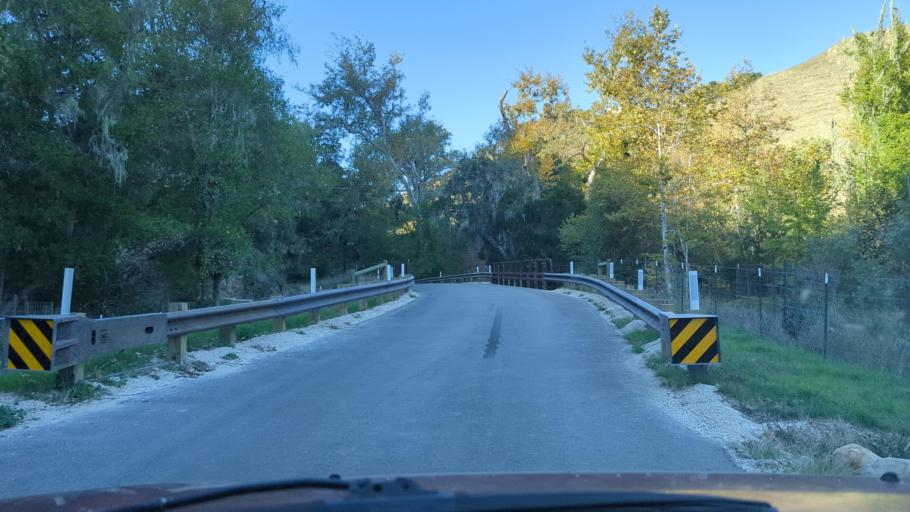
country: US
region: California
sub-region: Santa Barbara County
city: Santa Ynez
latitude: 34.5582
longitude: -120.0836
